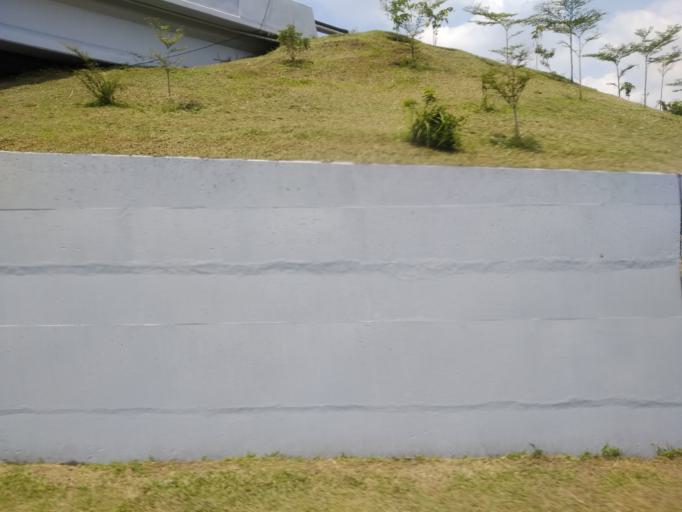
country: ID
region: West Java
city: Bogor
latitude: -6.5960
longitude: 106.8329
